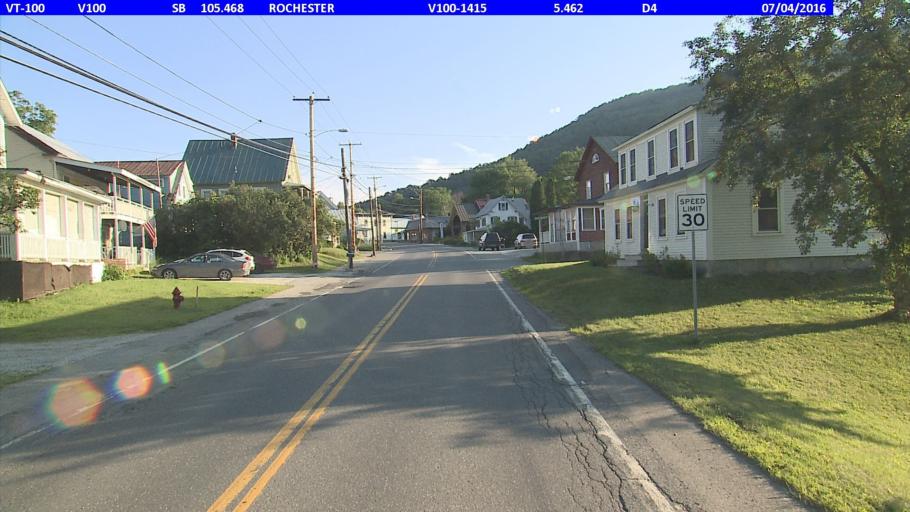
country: US
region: Vermont
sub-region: Orange County
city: Randolph
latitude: 43.8768
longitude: -72.8075
